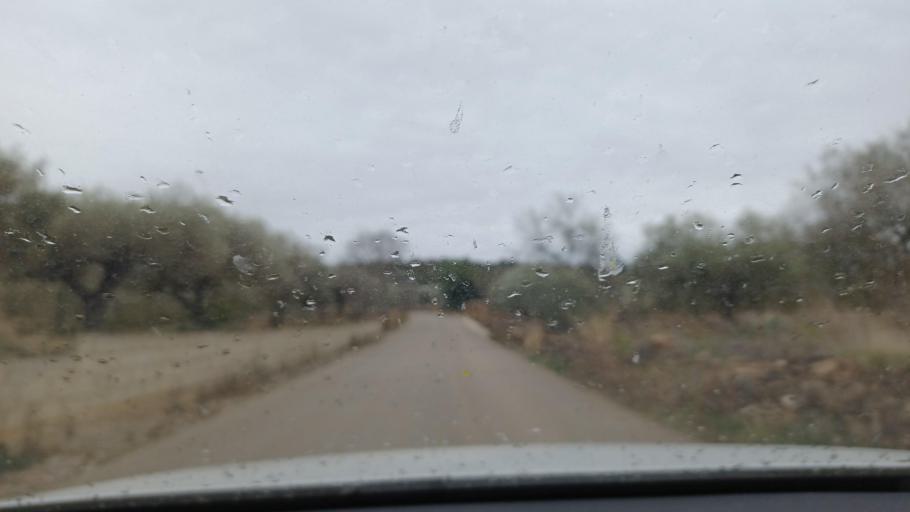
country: ES
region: Valencia
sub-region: Provincia de Castello
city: Traiguera
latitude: 40.5114
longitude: 0.2933
